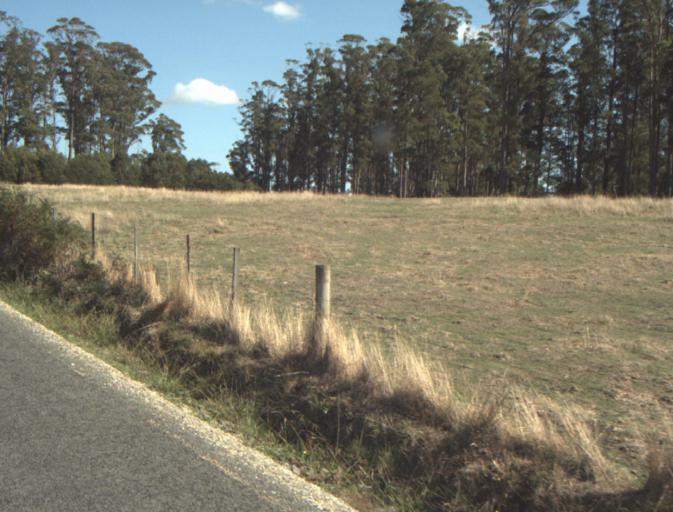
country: AU
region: Tasmania
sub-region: Launceston
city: Mayfield
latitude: -41.2317
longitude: 147.2353
